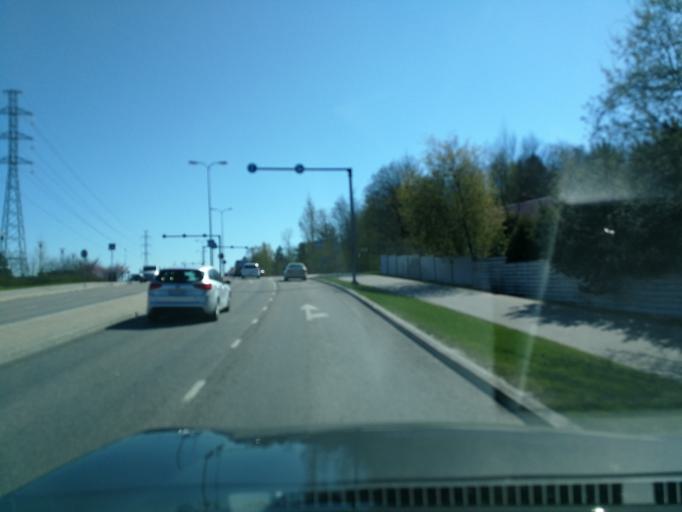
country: FI
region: Uusimaa
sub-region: Helsinki
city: Vantaa
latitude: 60.2788
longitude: 24.9705
